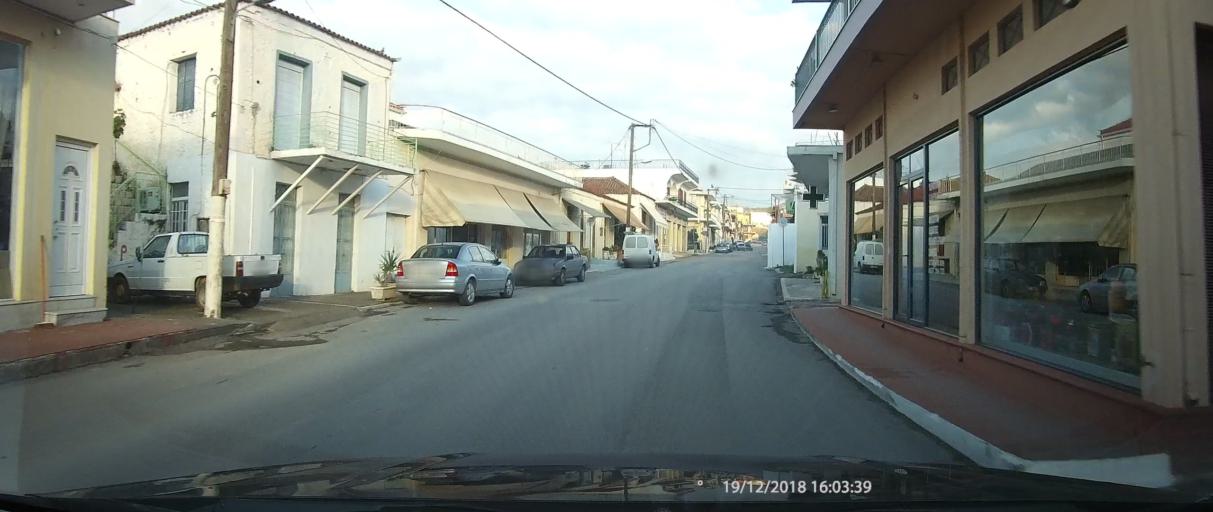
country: GR
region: Peloponnese
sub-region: Nomos Lakonias
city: Vlakhiotis
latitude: 36.8623
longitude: 22.7081
